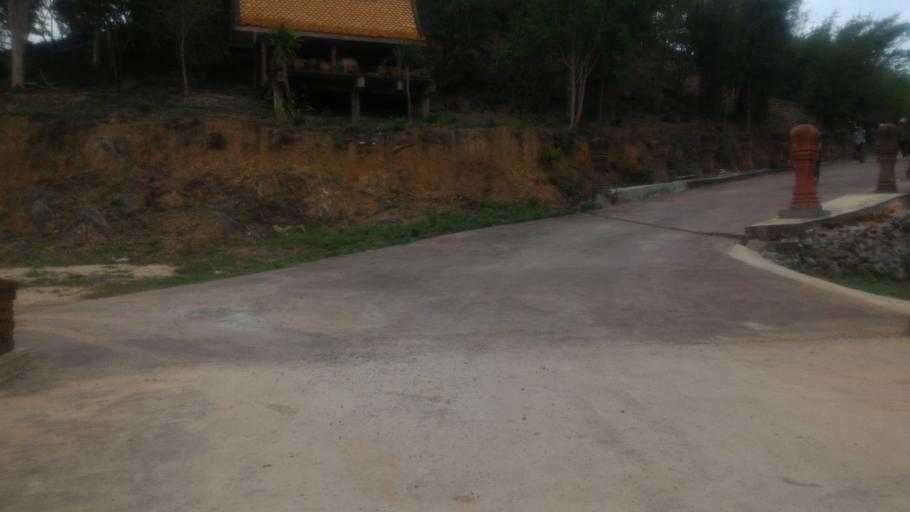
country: TH
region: Prachuap Khiri Khan
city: Kui Buri
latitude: 12.1087
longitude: 99.7545
